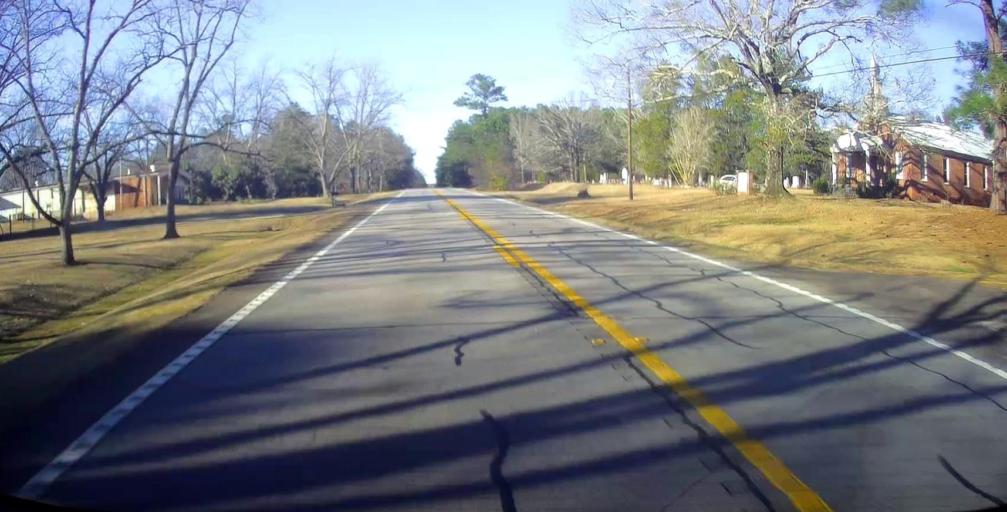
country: US
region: Georgia
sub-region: Meriwether County
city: Manchester
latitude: 32.8911
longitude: -84.5989
